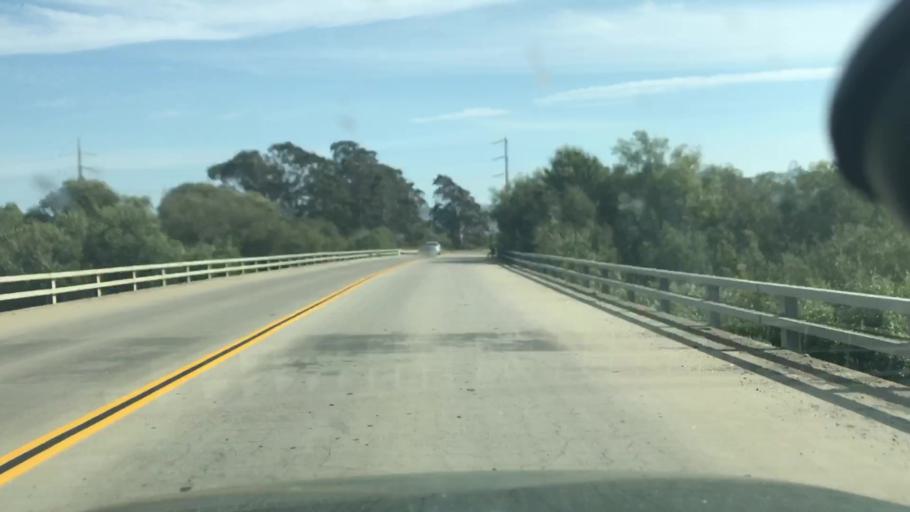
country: US
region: California
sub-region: Santa Barbara County
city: Vandenberg Village
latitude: 34.6725
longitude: -120.4933
